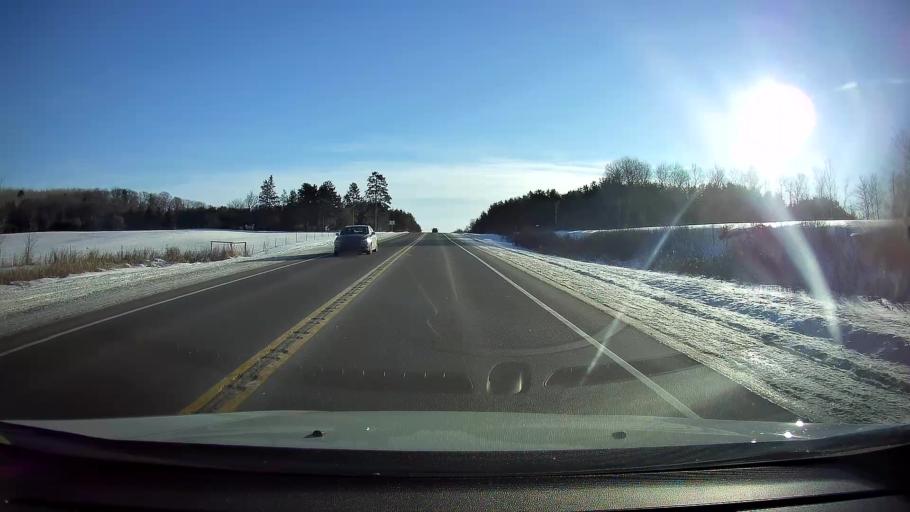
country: US
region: Wisconsin
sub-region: Sawyer County
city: Hayward
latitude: 45.9847
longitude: -91.5794
